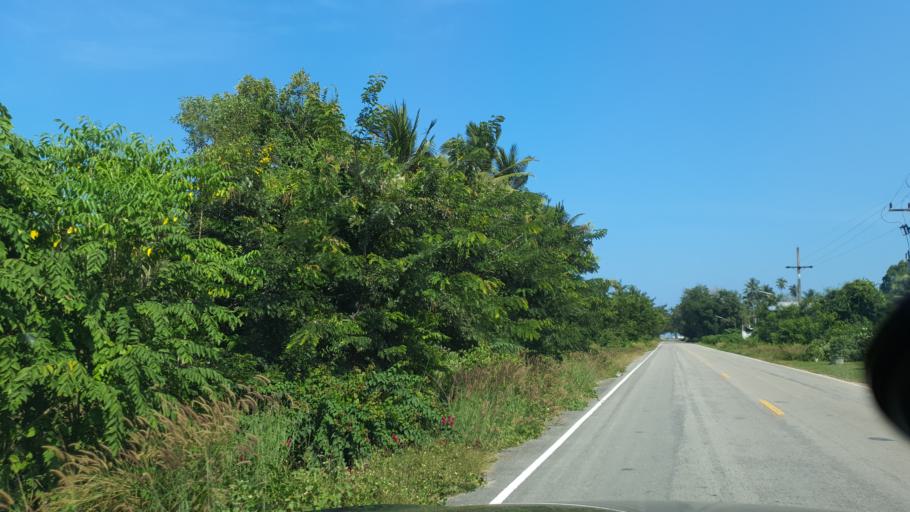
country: TH
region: Surat Thani
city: Tha Chana
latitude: 9.5875
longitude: 99.2037
